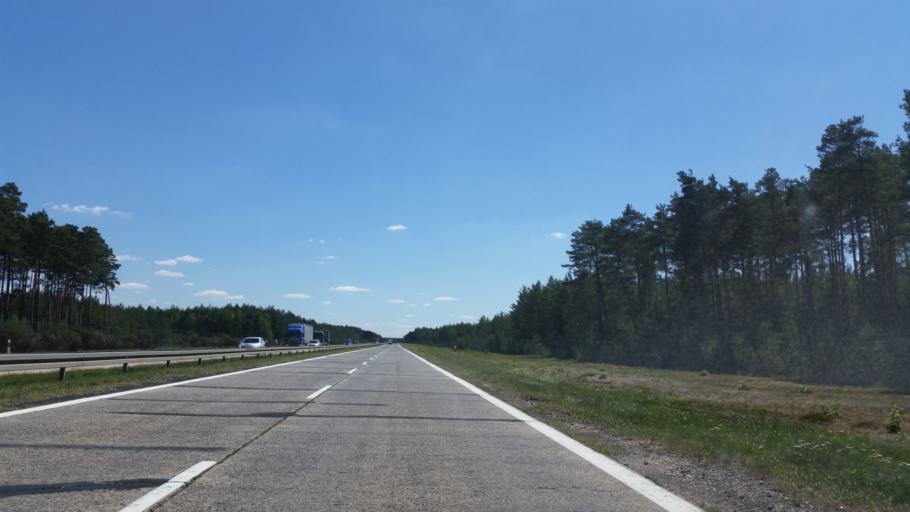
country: PL
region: Lower Silesian Voivodeship
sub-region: Powiat boleslawiecki
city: Boleslawiec
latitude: 51.3869
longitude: 15.5406
